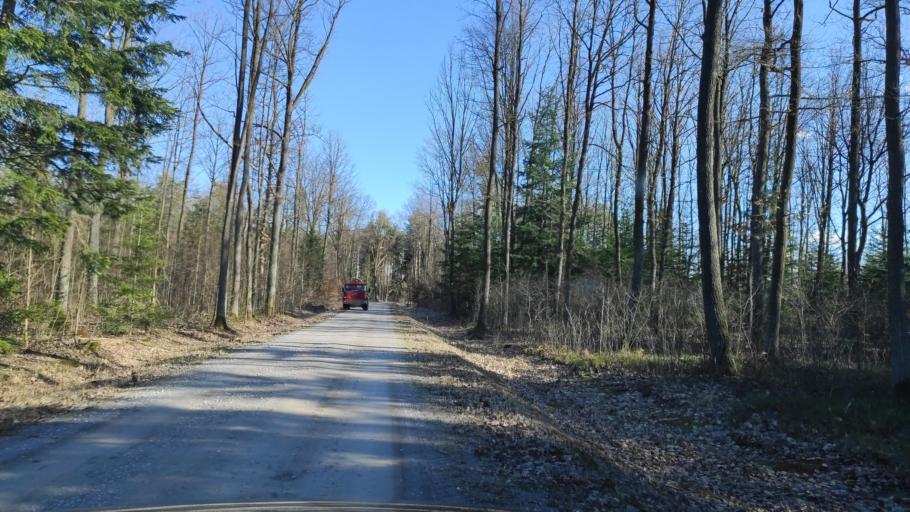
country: PL
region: Masovian Voivodeship
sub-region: Powiat radomski
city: Jedlnia-Letnisko
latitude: 51.4487
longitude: 21.2931
